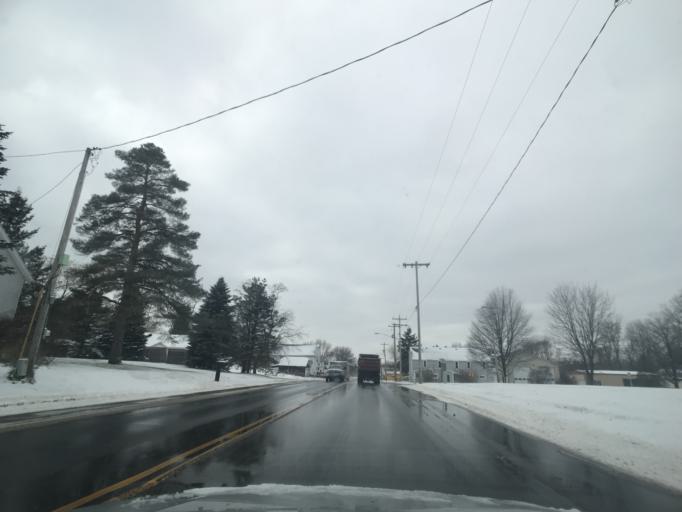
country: US
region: Wisconsin
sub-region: Brown County
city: Suamico
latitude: 44.7209
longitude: -88.0672
